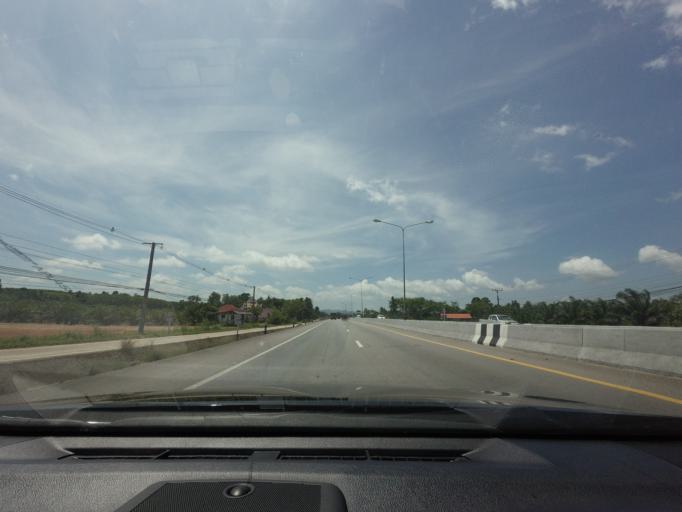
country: TH
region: Chumphon
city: Sawi
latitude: 10.2422
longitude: 99.0923
